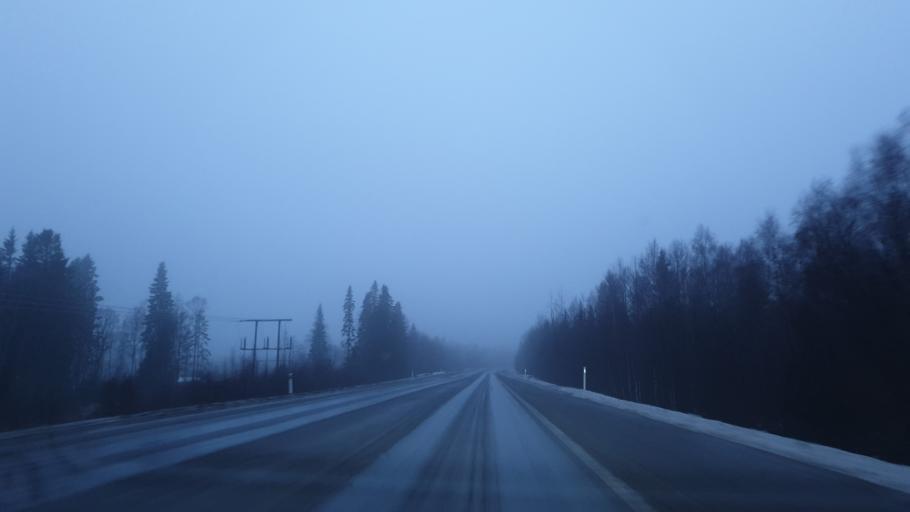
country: SE
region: Vaesterbotten
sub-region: Umea Kommun
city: Holmsund
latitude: 63.7524
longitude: 20.3652
